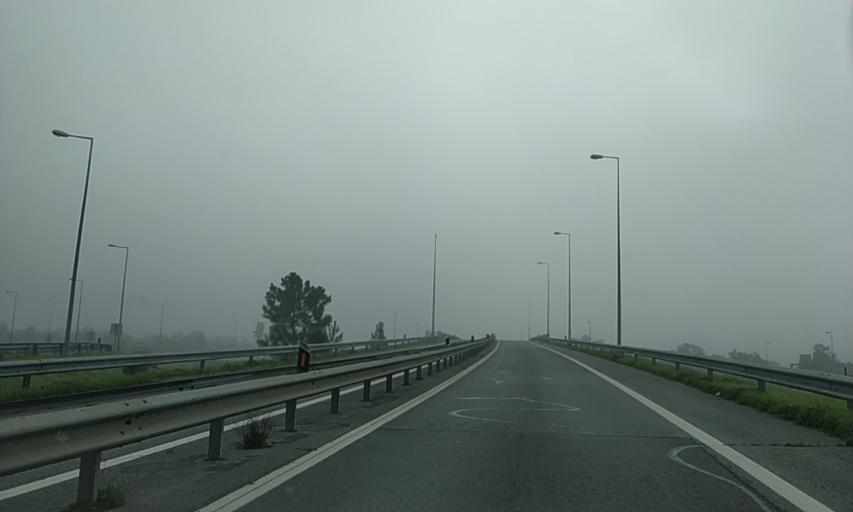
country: PT
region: Setubal
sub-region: Montijo
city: Montijo
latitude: 38.6797
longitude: -8.9462
